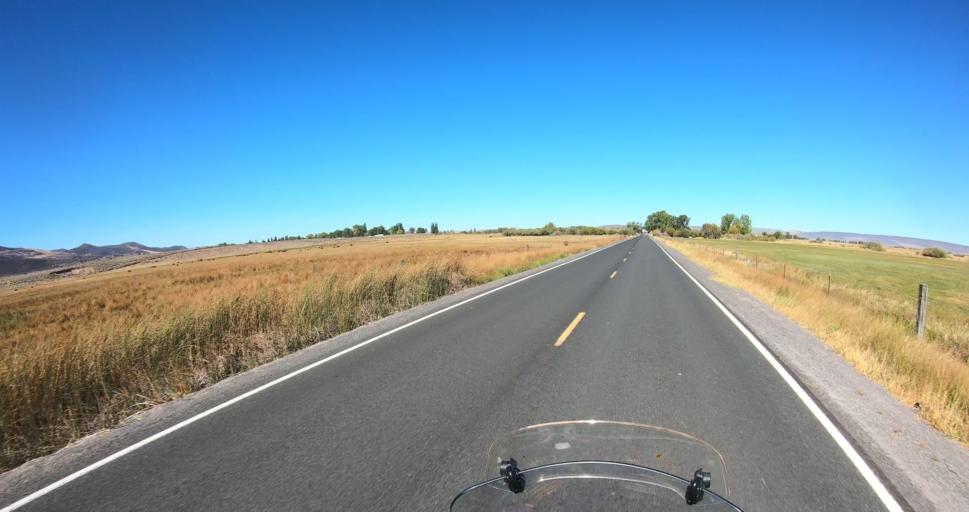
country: US
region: Oregon
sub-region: Lake County
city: Lakeview
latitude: 42.6793
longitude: -120.5284
